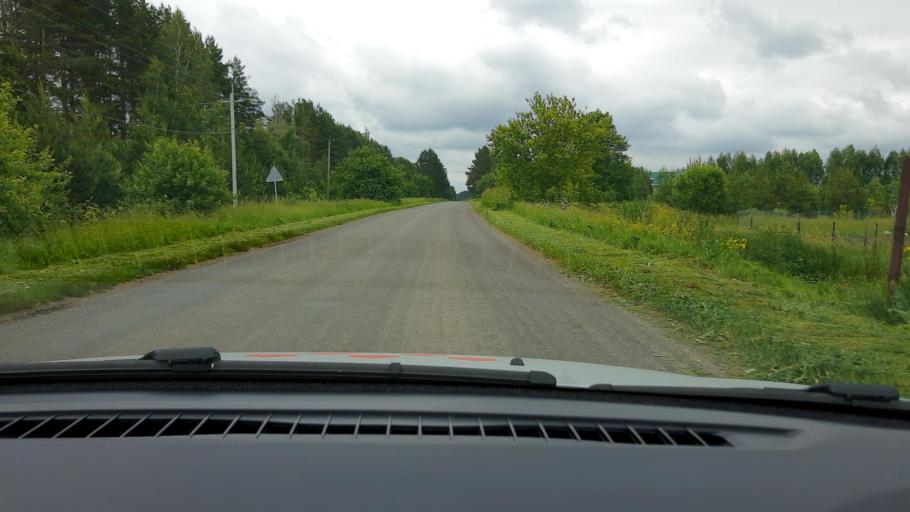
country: RU
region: Nizjnij Novgorod
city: Bogorodsk
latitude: 56.0272
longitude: 43.4588
